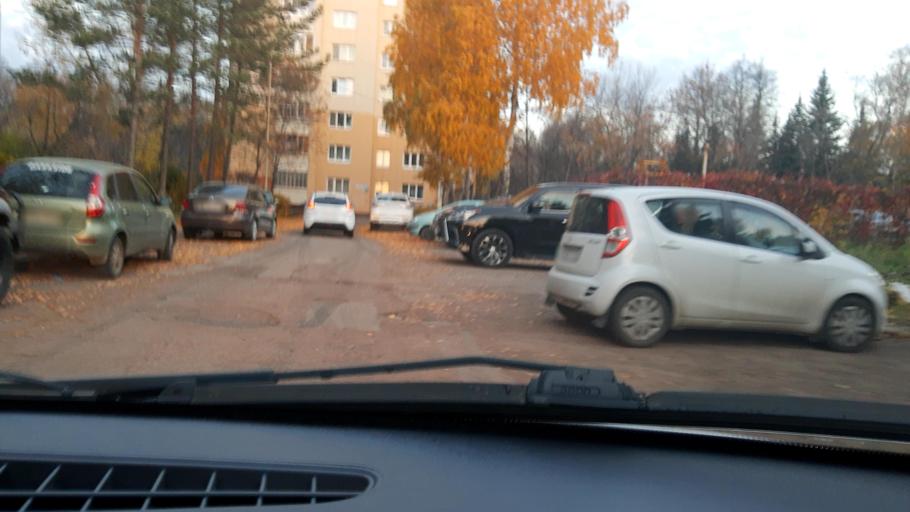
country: RU
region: Bashkortostan
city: Ufa
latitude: 54.7568
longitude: 55.9921
